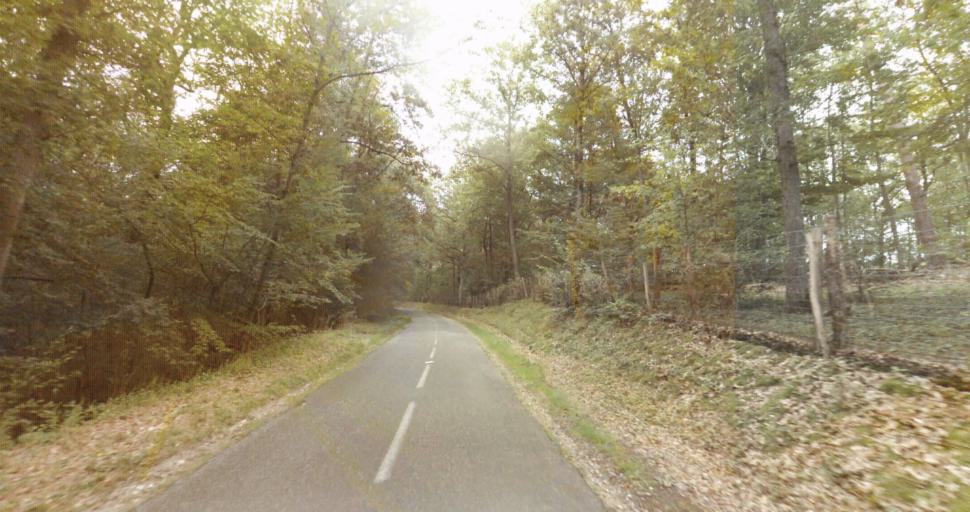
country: FR
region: Haute-Normandie
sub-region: Departement de l'Eure
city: Croth
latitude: 48.8604
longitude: 1.3542
